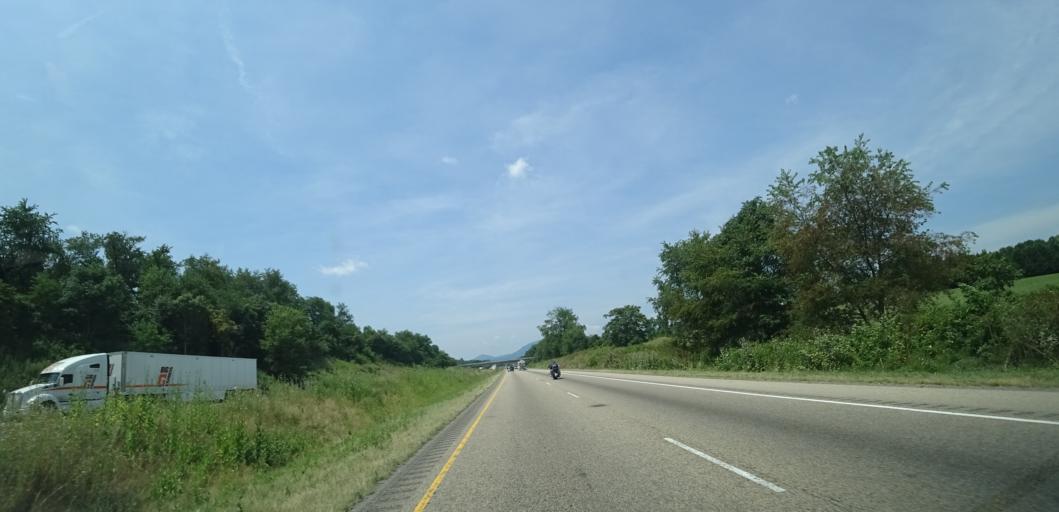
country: US
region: Virginia
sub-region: Rockbridge County
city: Glasgow
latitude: 37.6620
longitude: -79.5252
